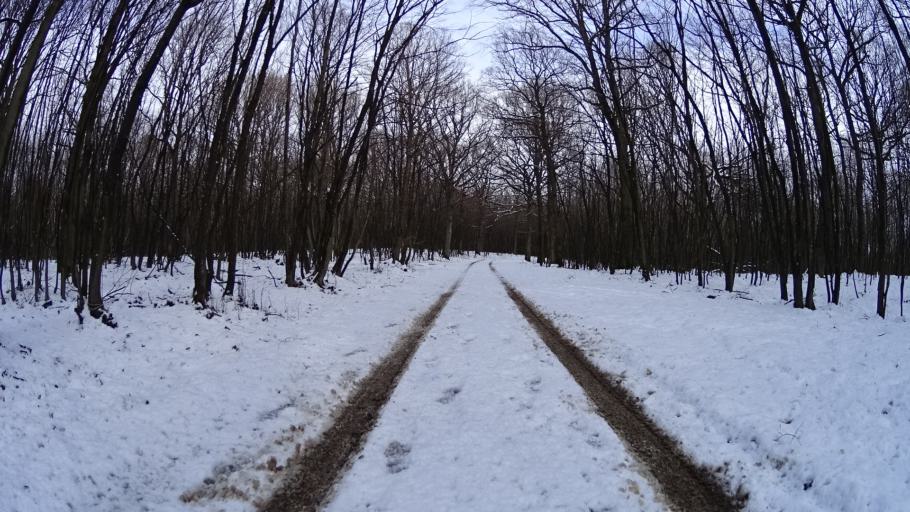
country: AT
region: Lower Austria
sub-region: Politischer Bezirk Korneuburg
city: Leobendorf
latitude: 48.4142
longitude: 16.3359
